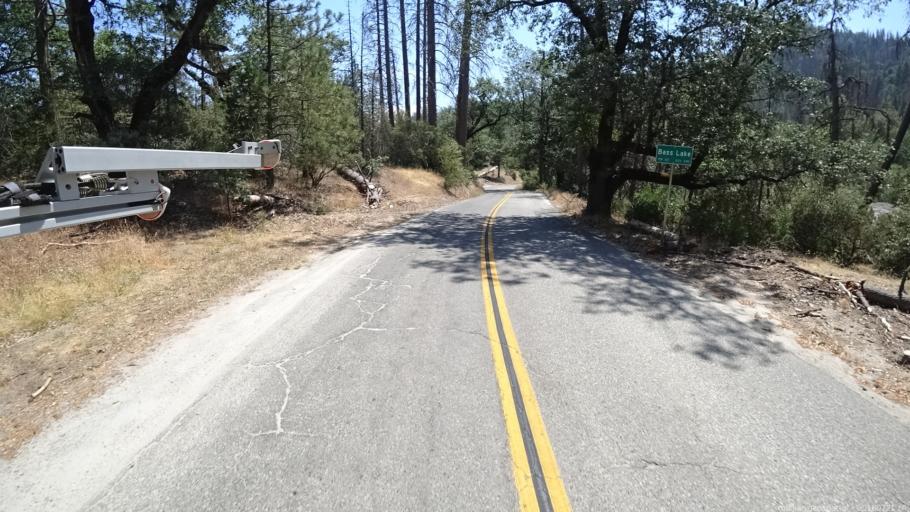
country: US
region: California
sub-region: Madera County
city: Oakhurst
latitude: 37.3120
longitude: -119.5733
